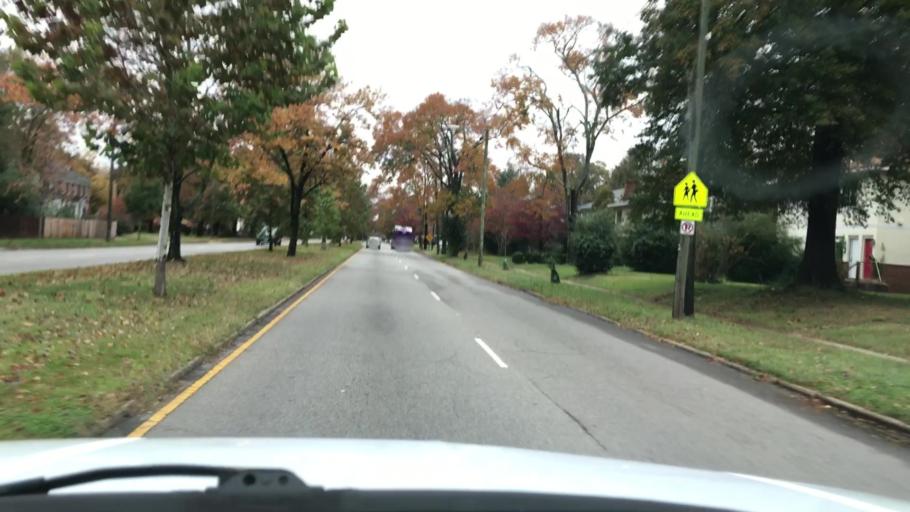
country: US
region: Virginia
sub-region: Henrico County
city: Lakeside
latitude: 37.5931
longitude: -77.4487
